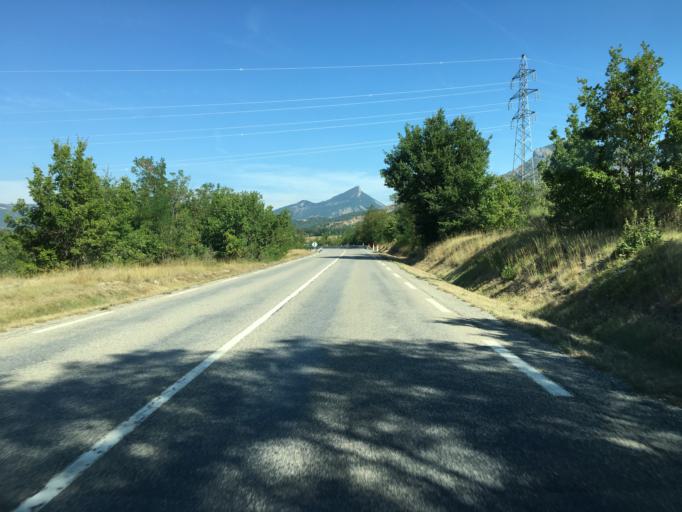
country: FR
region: Provence-Alpes-Cote d'Azur
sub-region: Departement des Hautes-Alpes
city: Laragne-Monteglin
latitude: 44.3555
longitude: 5.7648
